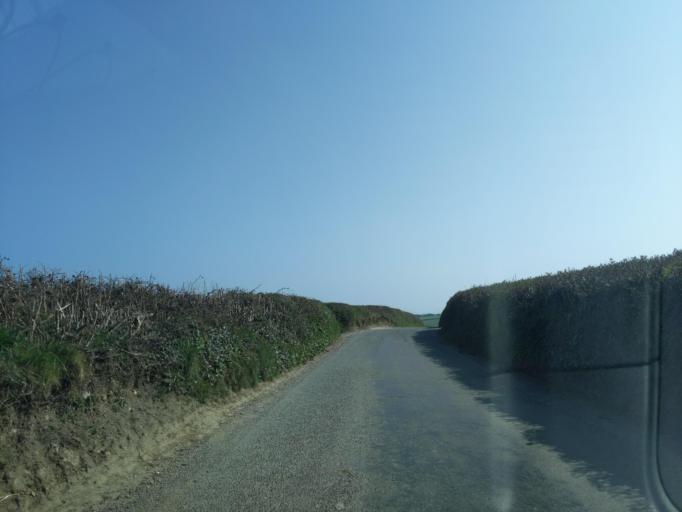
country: GB
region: England
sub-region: Devon
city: Dartmouth
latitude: 50.3294
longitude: -3.6436
